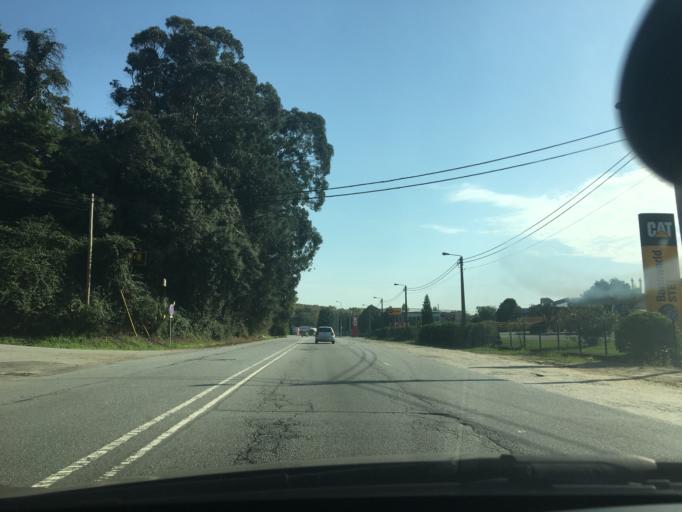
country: PT
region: Porto
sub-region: Maia
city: Maia
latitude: 41.2328
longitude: -8.6379
